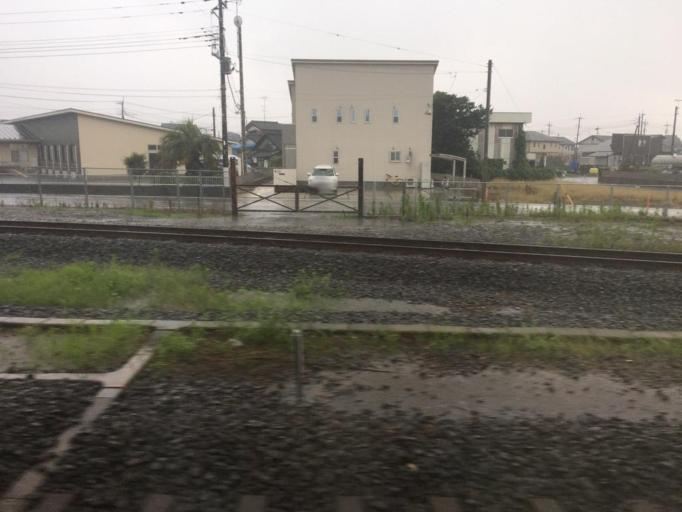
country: JP
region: Gunma
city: Tatebayashi
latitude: 36.2741
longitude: 139.4997
